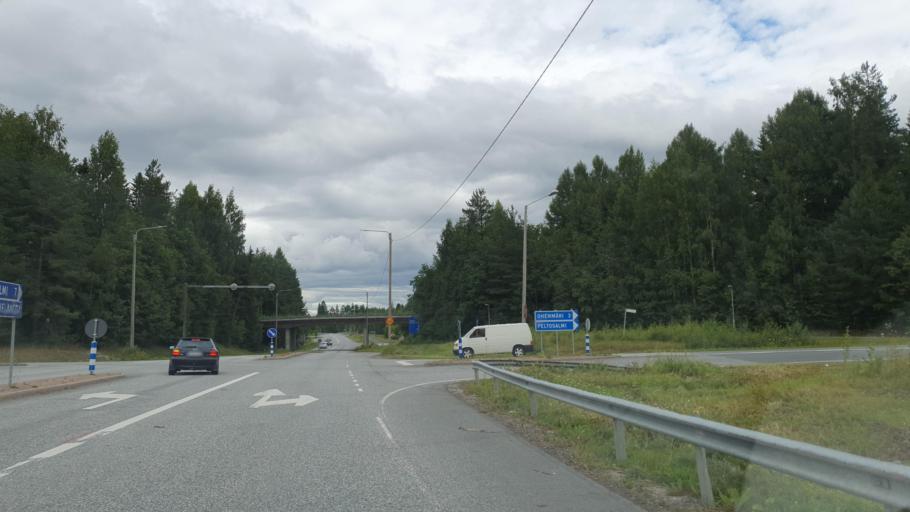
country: FI
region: Northern Savo
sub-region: Ylae-Savo
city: Iisalmi
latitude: 63.5221
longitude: 27.2426
